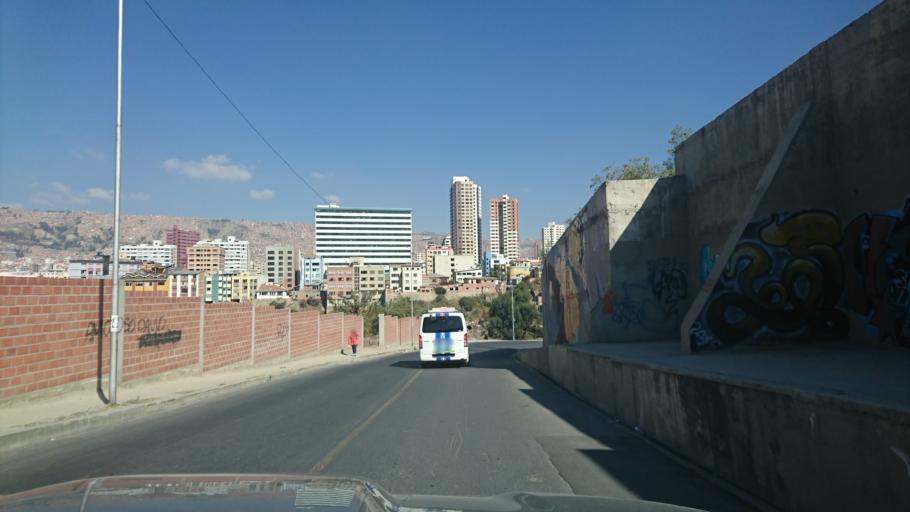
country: BO
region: La Paz
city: La Paz
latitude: -16.5017
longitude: -68.1144
